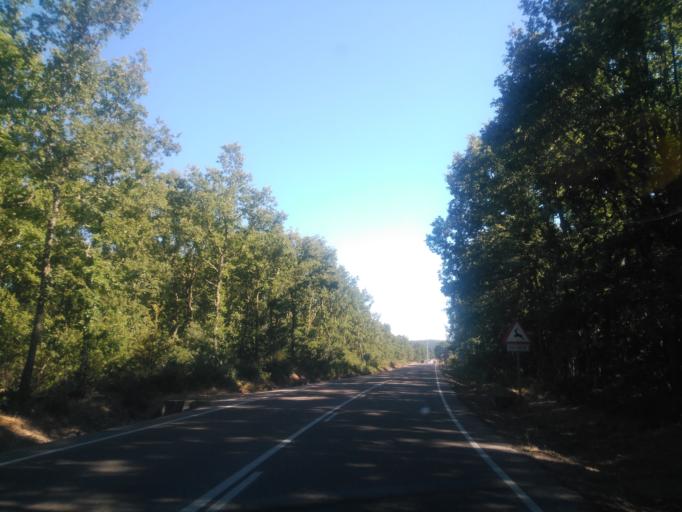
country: ES
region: Castille and Leon
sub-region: Provincia de Zamora
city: Galende
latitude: 42.0964
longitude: -6.6479
